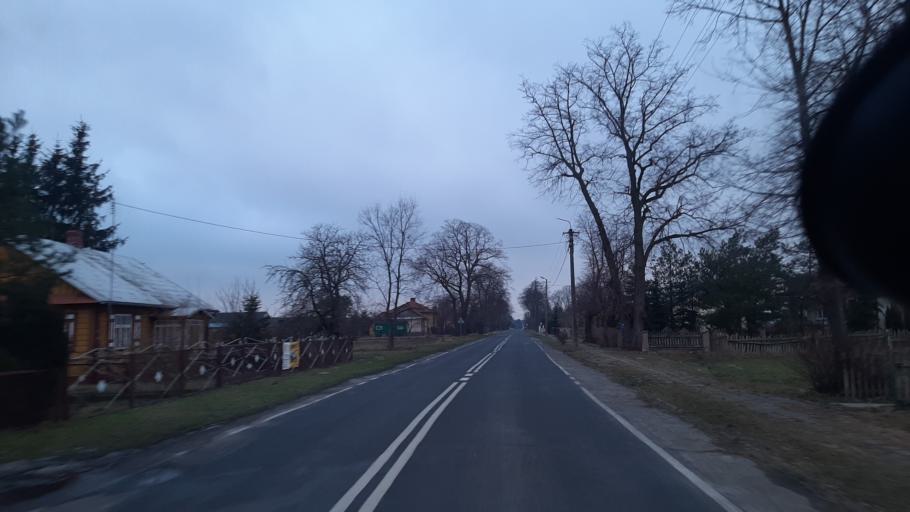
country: PL
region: Lublin Voivodeship
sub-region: Powiat parczewski
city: Debowa Kloda
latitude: 51.6370
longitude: 23.0498
